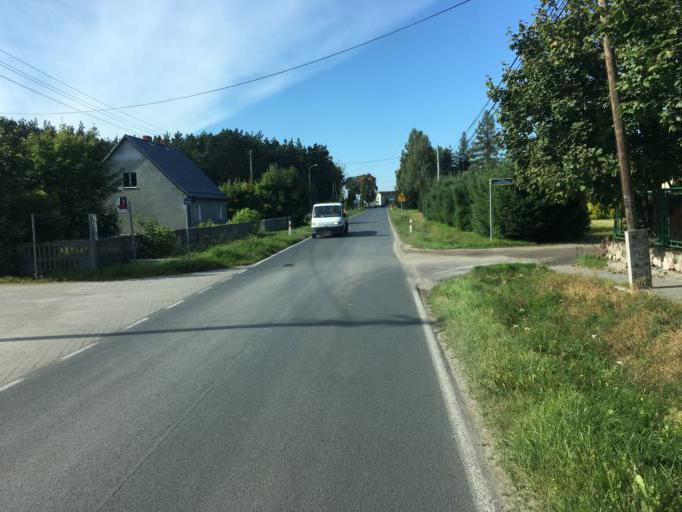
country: PL
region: Kujawsko-Pomorskie
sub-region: Powiat swiecki
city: Lniano
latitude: 53.5255
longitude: 18.2083
